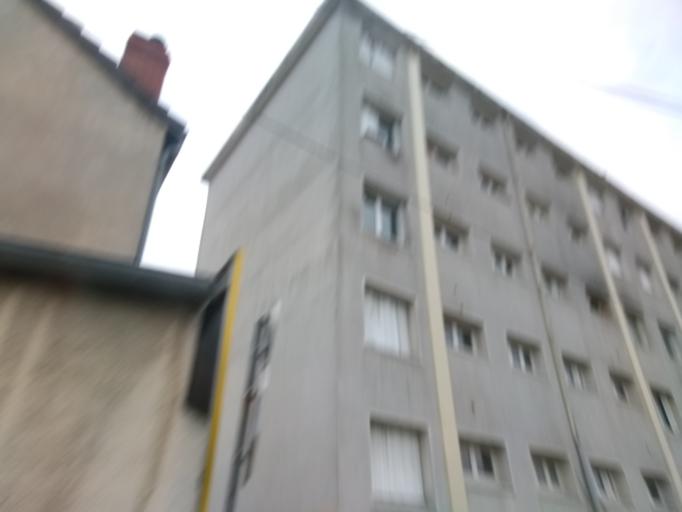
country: FR
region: Picardie
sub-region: Departement de l'Oise
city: Venette
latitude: 49.3953
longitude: 2.8022
